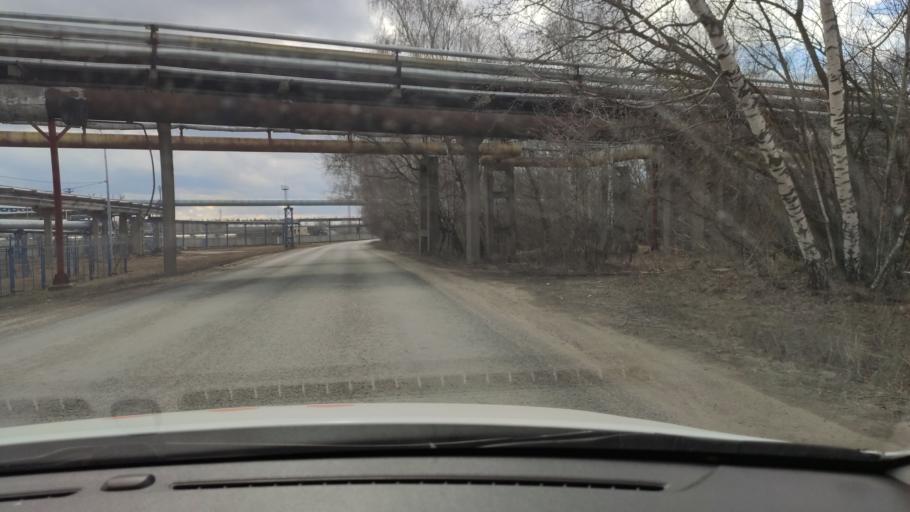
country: RU
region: Tatarstan
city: Staroye Arakchino
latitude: 55.8655
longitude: 48.9718
